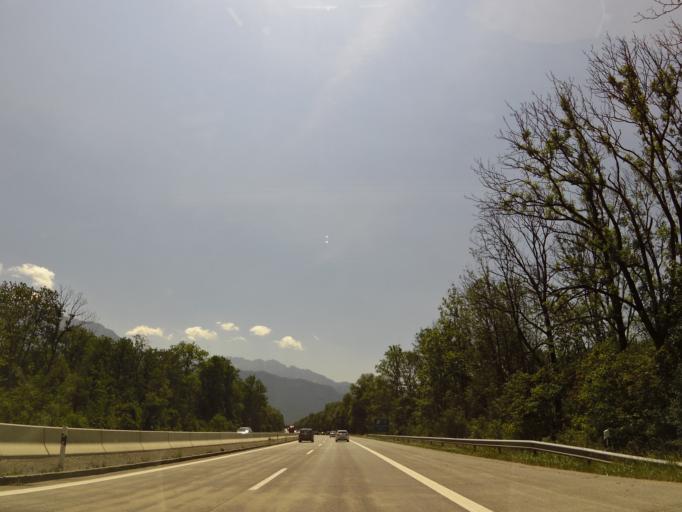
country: DE
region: Bavaria
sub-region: Upper Bavaria
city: Oberaudorf
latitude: 47.6574
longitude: 12.1842
